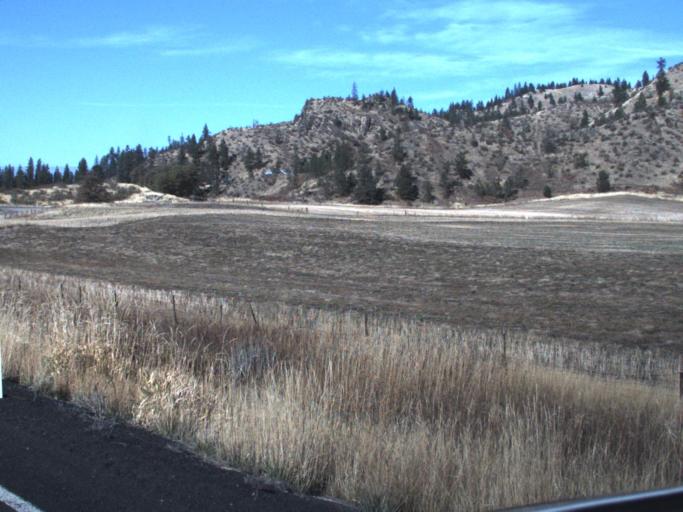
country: US
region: Washington
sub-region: Lincoln County
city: Davenport
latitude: 47.8916
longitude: -118.2699
